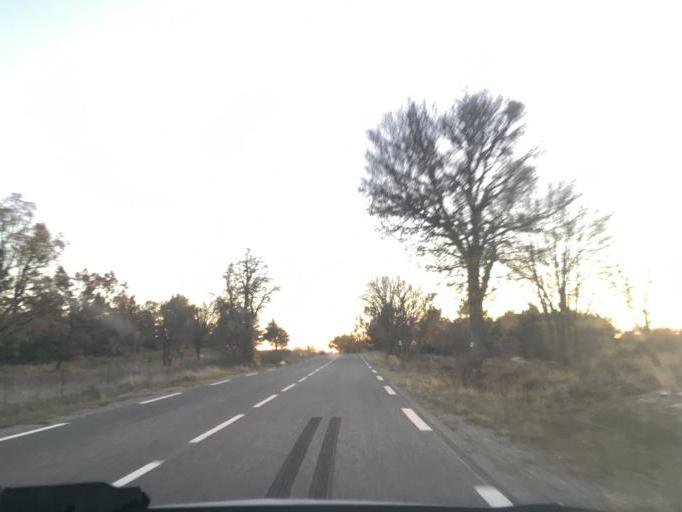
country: FR
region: Provence-Alpes-Cote d'Azur
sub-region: Departement du Var
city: Montferrat
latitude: 43.6543
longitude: 6.4785
